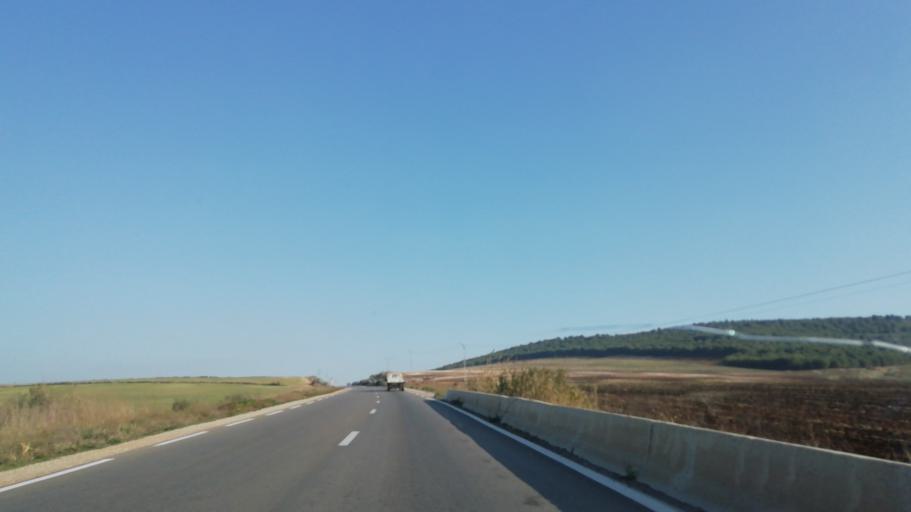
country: DZ
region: Ain Temouchent
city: Hammam Bou Hadjar
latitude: 35.1666
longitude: -0.8921
